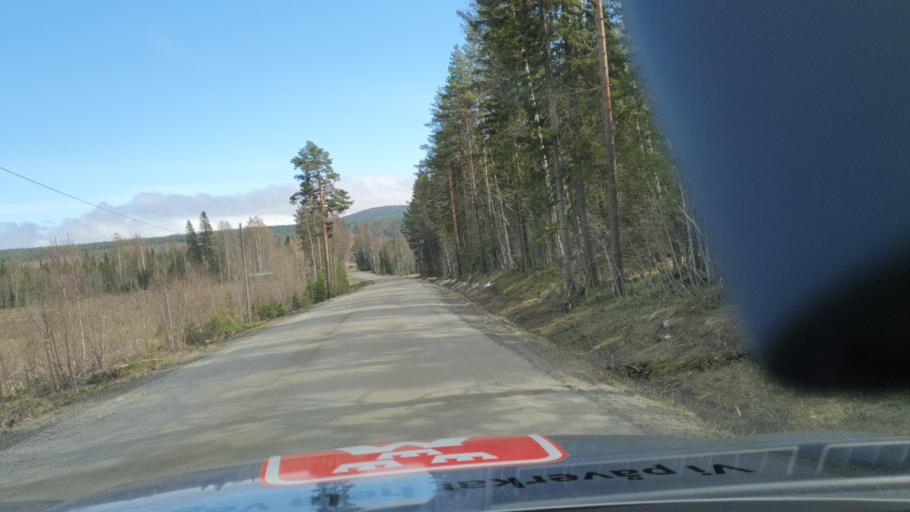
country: SE
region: Vaesterbotten
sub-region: Bjurholms Kommun
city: Bjurholm
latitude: 63.7007
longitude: 18.9302
